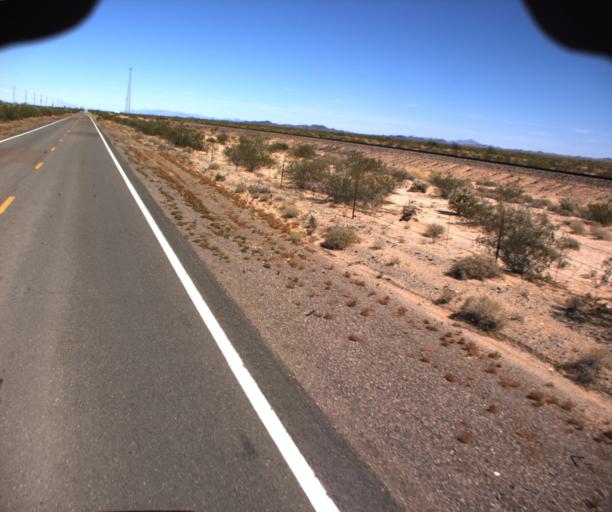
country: US
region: Arizona
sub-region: La Paz County
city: Salome
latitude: 33.8319
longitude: -113.8777
